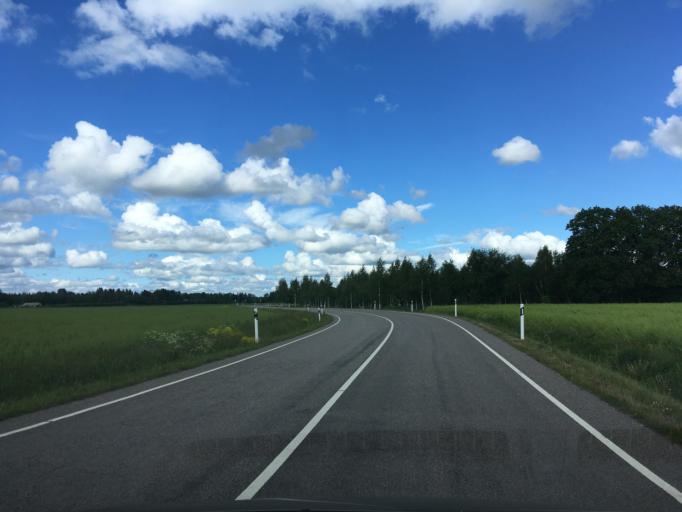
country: EE
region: Paernumaa
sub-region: Tootsi vald
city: Tootsi
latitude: 58.6542
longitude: 24.7093
